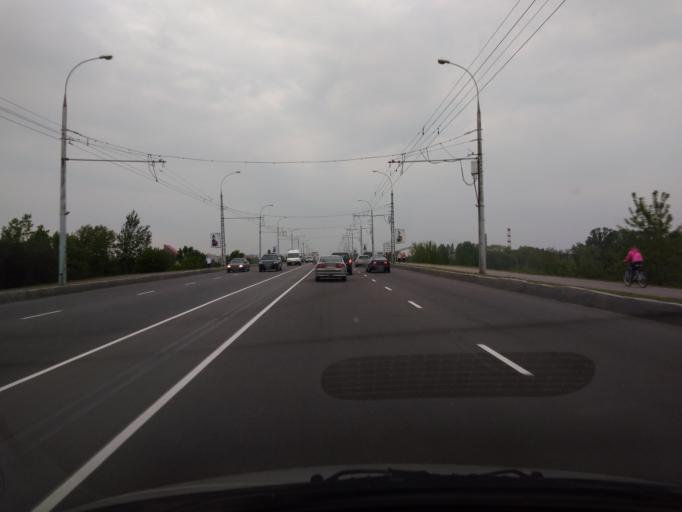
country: BY
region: Brest
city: Brest
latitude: 52.0850
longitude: 23.7357
